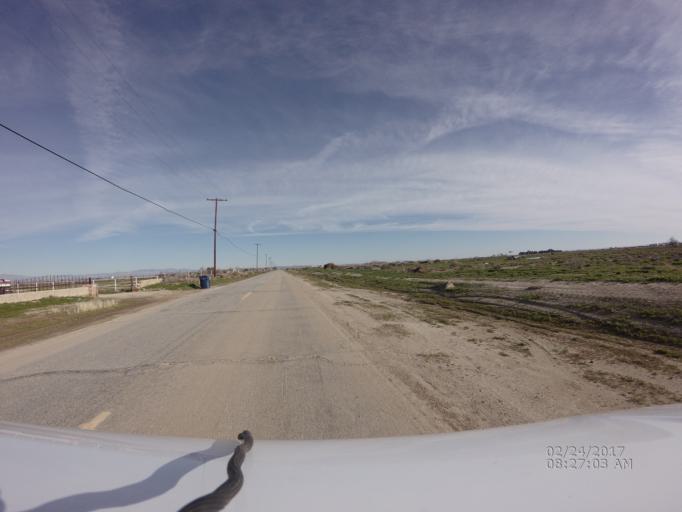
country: US
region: California
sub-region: Los Angeles County
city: Lancaster
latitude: 34.7269
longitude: -118.0233
